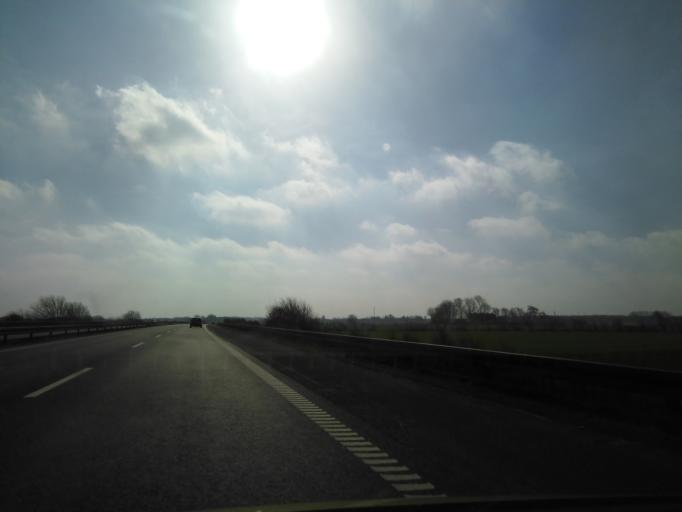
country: DK
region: South Denmark
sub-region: Fredericia Kommune
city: Taulov
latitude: 55.5795
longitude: 9.6130
